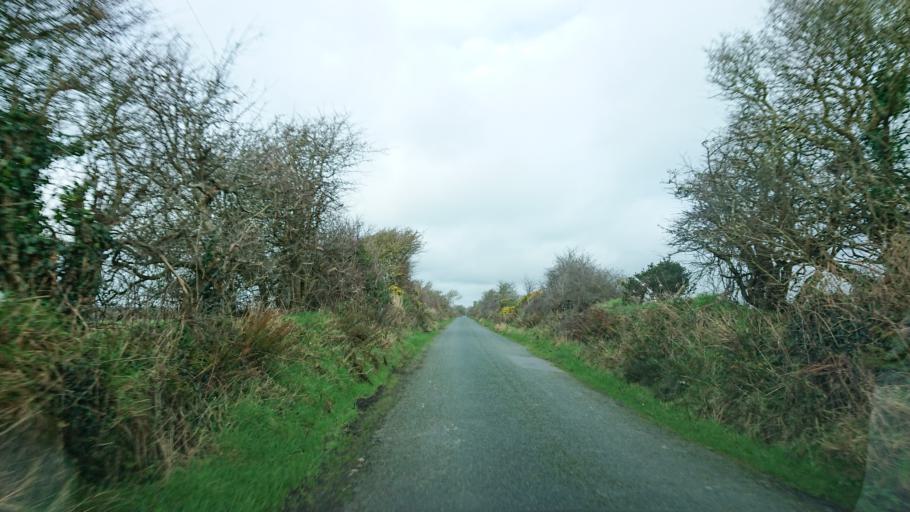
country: IE
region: Munster
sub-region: Waterford
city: Portlaw
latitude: 52.1568
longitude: -7.3085
